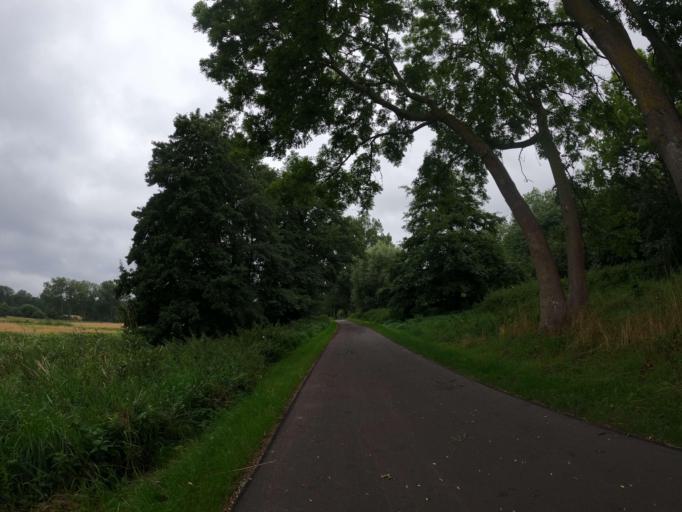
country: DE
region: Mecklenburg-Vorpommern
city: Poseritz
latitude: 54.2835
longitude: 13.2333
